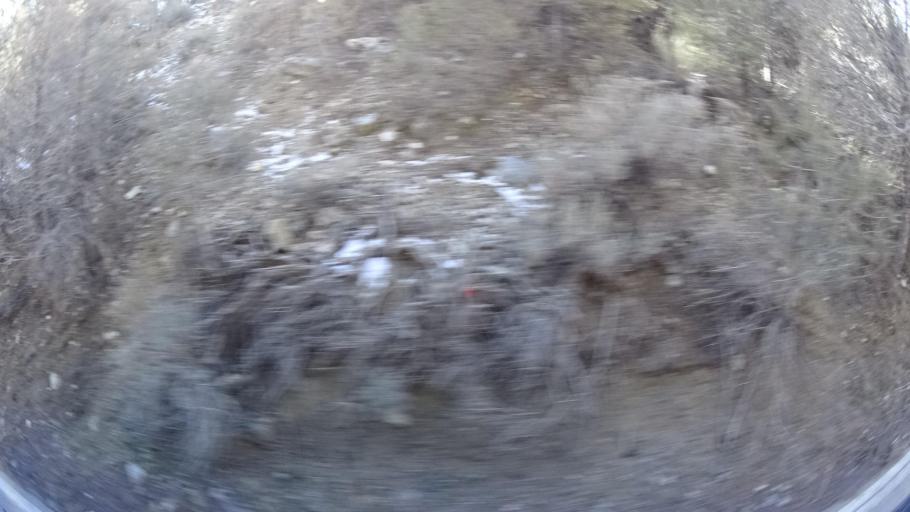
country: US
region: California
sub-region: Kern County
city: Pine Mountain Club
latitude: 34.8535
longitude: -119.1337
